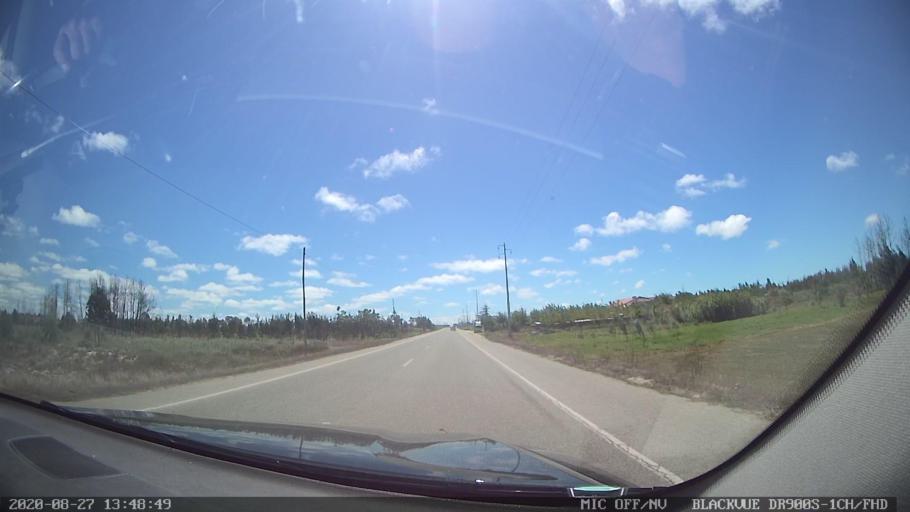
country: PT
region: Coimbra
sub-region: Mira
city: Mira
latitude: 40.3733
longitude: -8.7455
